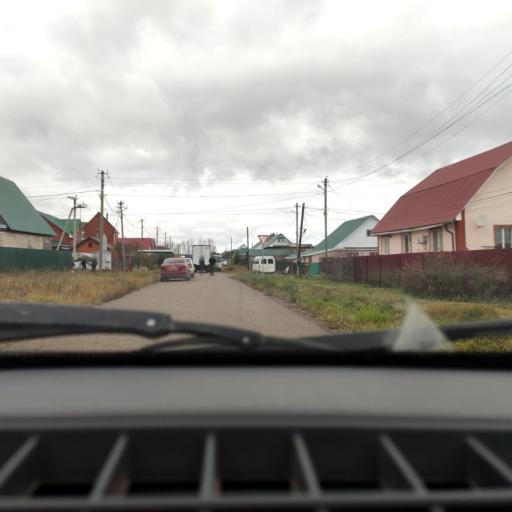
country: RU
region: Bashkortostan
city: Mikhaylovka
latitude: 54.8198
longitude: 55.8901
